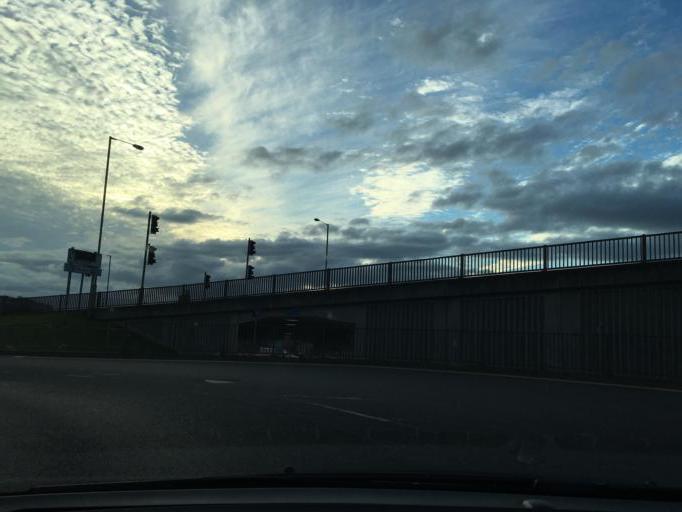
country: GB
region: Scotland
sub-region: Highland
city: Inverness
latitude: 57.4821
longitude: -4.2248
